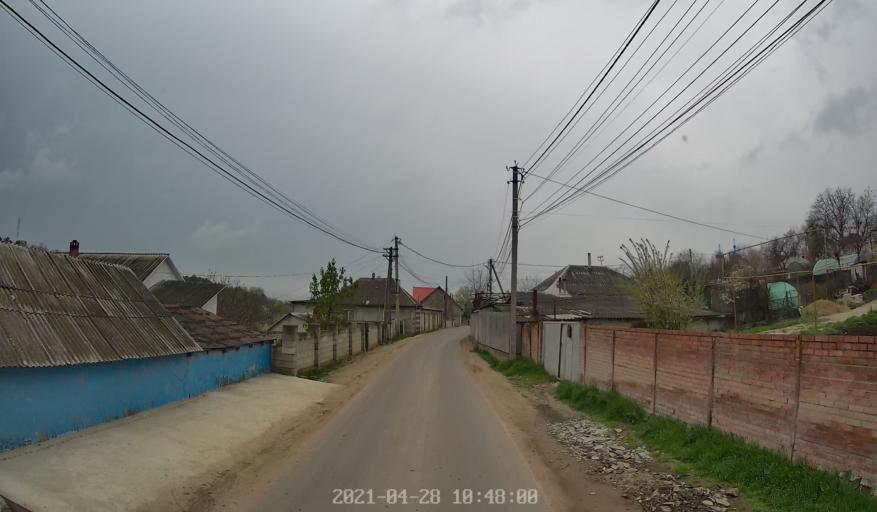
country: MD
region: Chisinau
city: Singera
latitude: 46.9863
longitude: 28.9458
